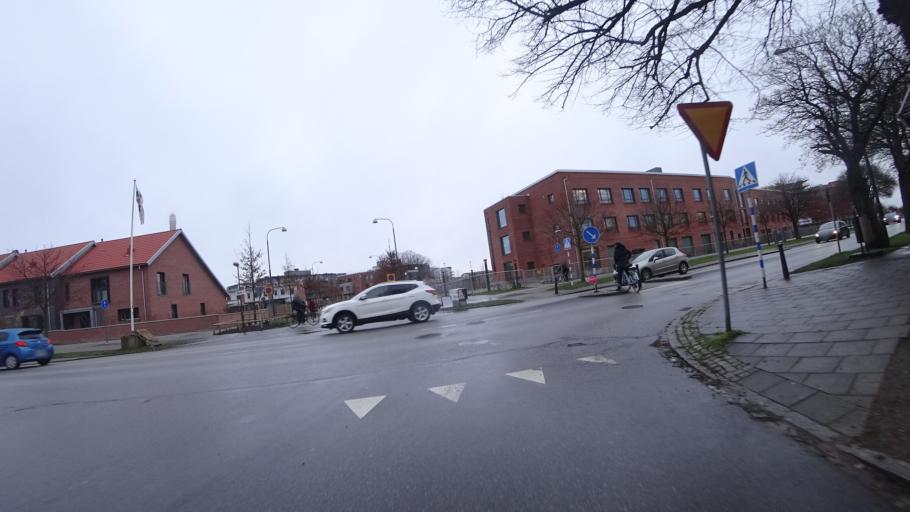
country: SE
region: Skane
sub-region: Malmo
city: Bunkeflostrand
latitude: 55.5868
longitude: 12.9351
